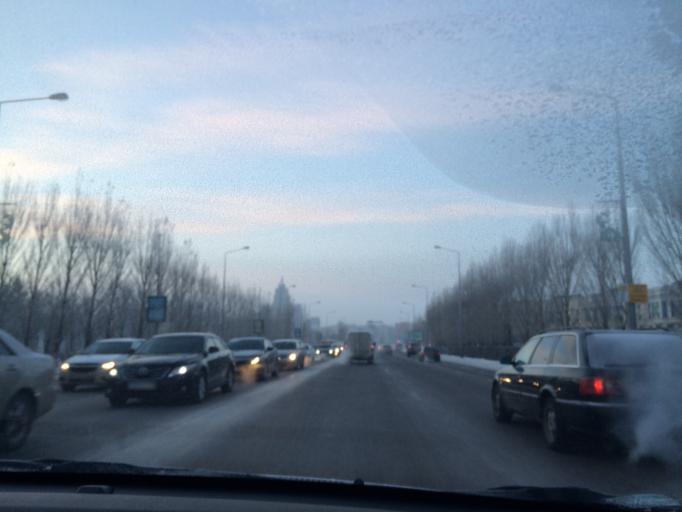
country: KZ
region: Astana Qalasy
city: Astana
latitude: 51.1511
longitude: 71.4125
